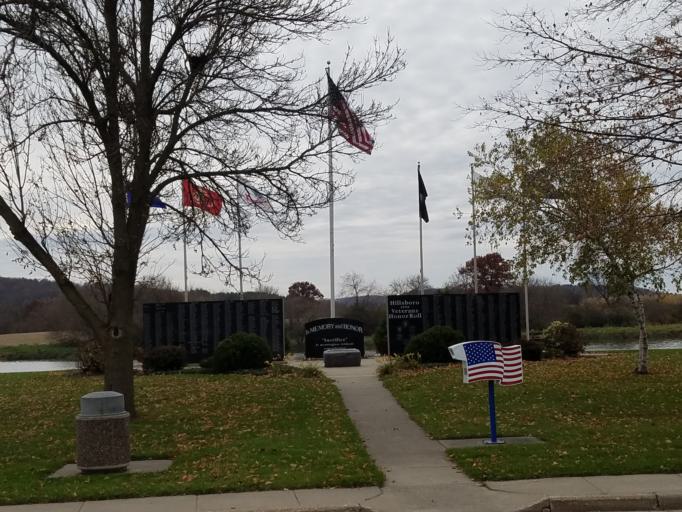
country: US
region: Wisconsin
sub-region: Vernon County
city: Hillsboro
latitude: 43.6491
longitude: -90.3478
